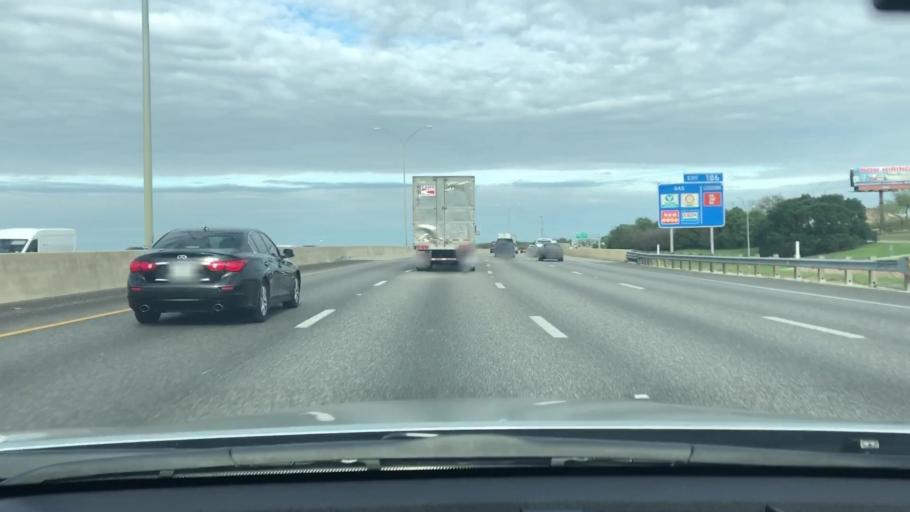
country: US
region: Texas
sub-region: Comal County
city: New Braunfels
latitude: 29.6813
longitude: -98.1437
